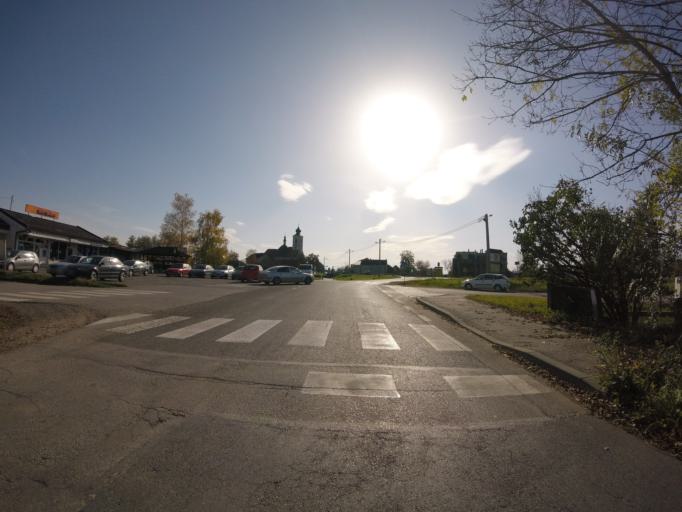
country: HR
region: Zagrebacka
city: Mraclin
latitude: 45.6870
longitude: 16.1159
